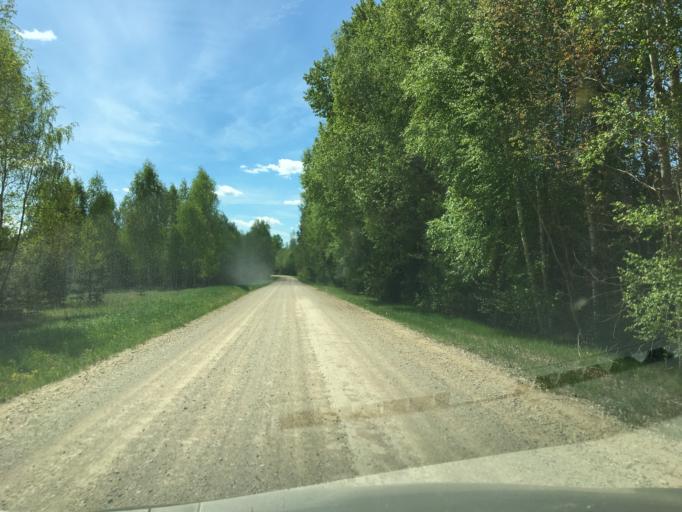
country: EE
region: Vorumaa
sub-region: Antsla vald
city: Vana-Antsla
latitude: 57.8973
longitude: 26.3532
